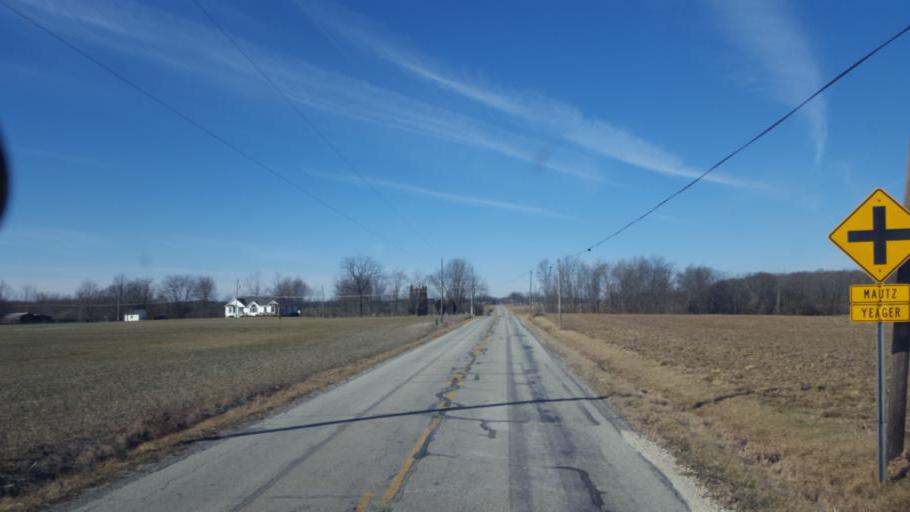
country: US
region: Ohio
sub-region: Marion County
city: Marion
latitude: 40.5276
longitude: -83.0374
